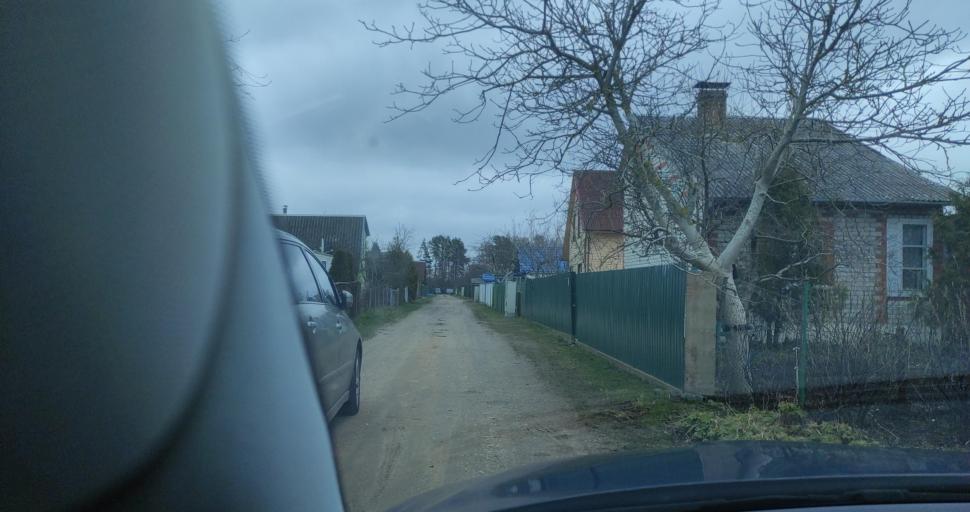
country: LV
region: Liepaja
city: Vec-Liepaja
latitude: 56.6141
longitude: 21.0435
